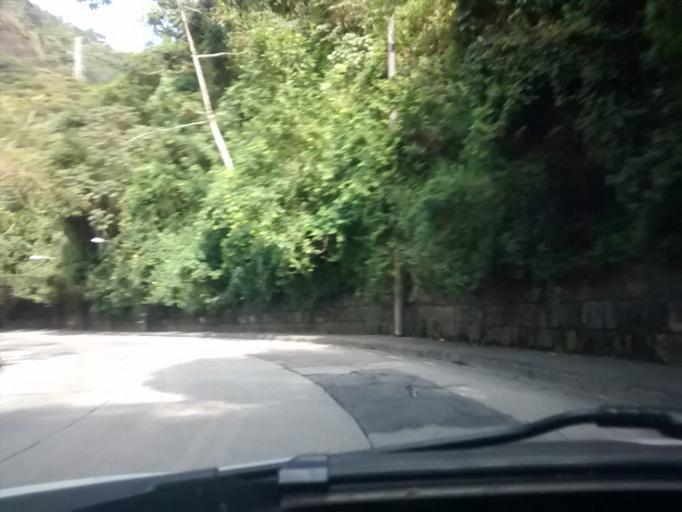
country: BR
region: Rio de Janeiro
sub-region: Rio De Janeiro
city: Rio de Janeiro
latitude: -22.9584
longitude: -43.2653
